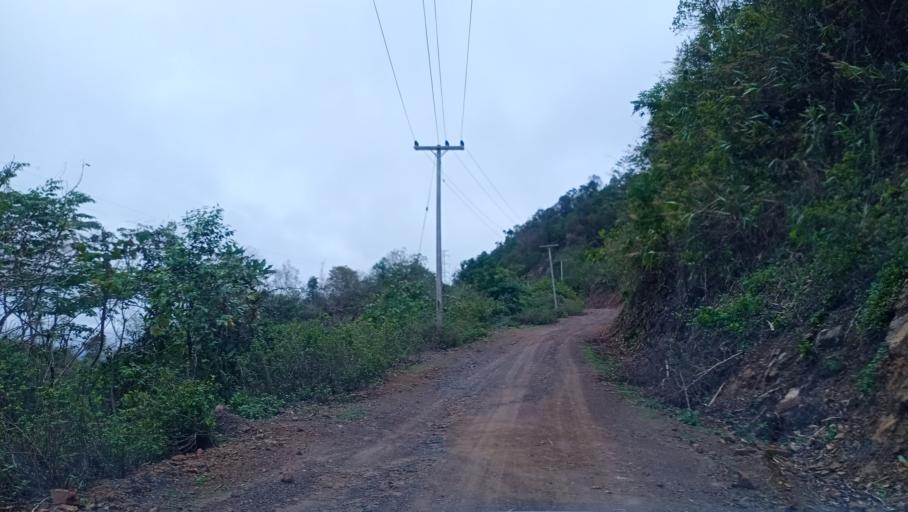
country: LA
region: Phongsali
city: Phongsali
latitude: 21.3494
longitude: 102.0965
